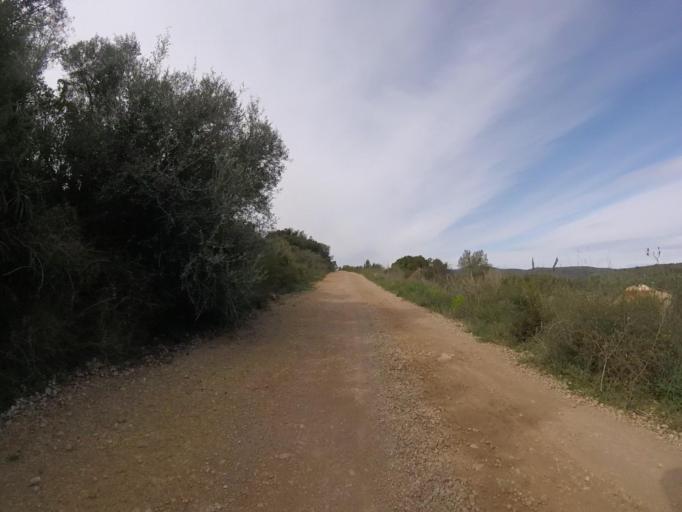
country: ES
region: Valencia
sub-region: Provincia de Castello
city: Torreblanca
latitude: 40.2011
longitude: 0.1368
